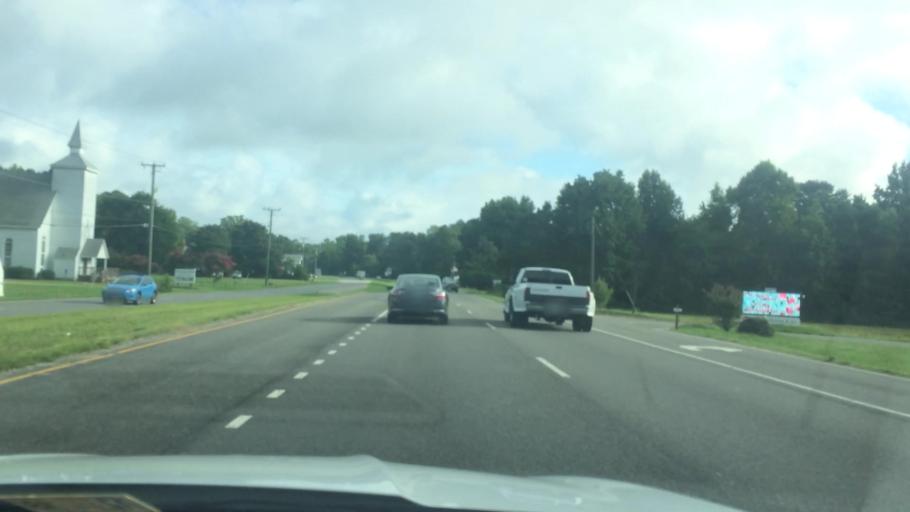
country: US
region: Virginia
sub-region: Gloucester County
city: Gloucester Point
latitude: 37.3293
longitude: -76.5144
